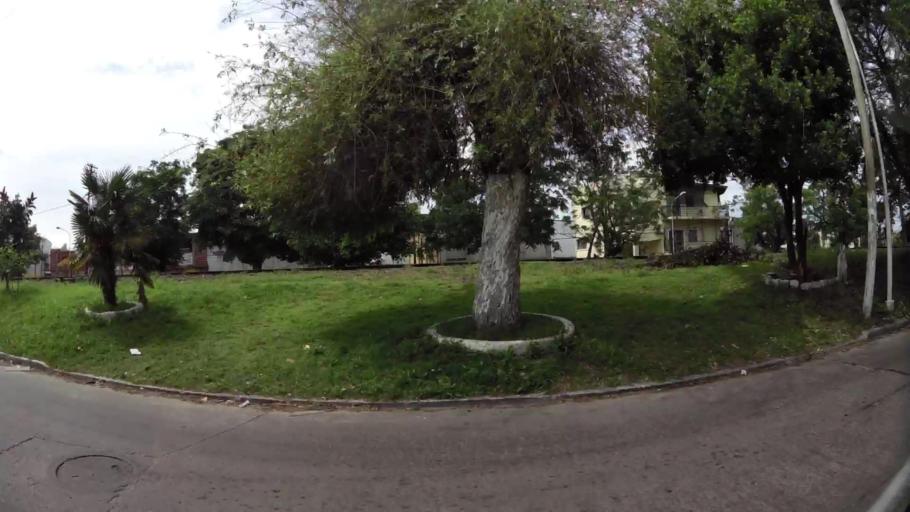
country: AR
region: Buenos Aires F.D.
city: Villa Lugano
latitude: -34.6858
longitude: -58.4975
